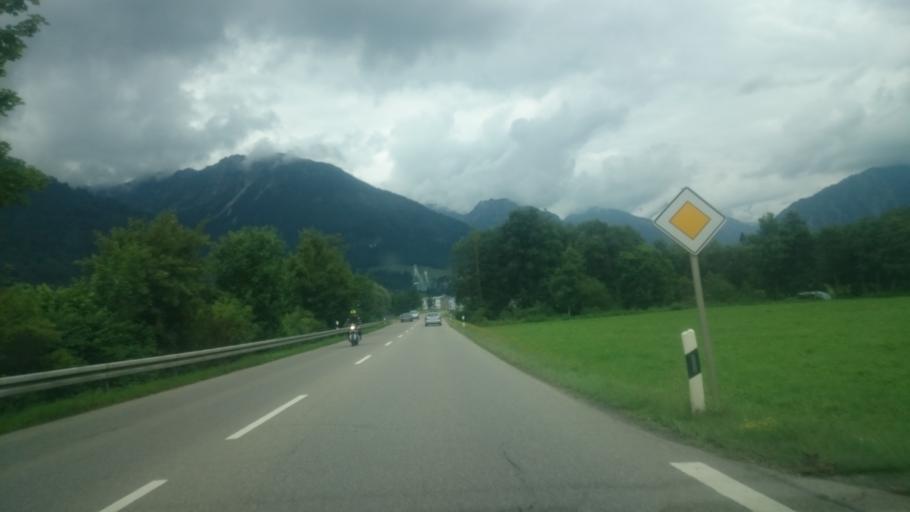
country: DE
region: Bavaria
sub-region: Swabia
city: Oberstdorf
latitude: 47.4232
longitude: 10.2693
